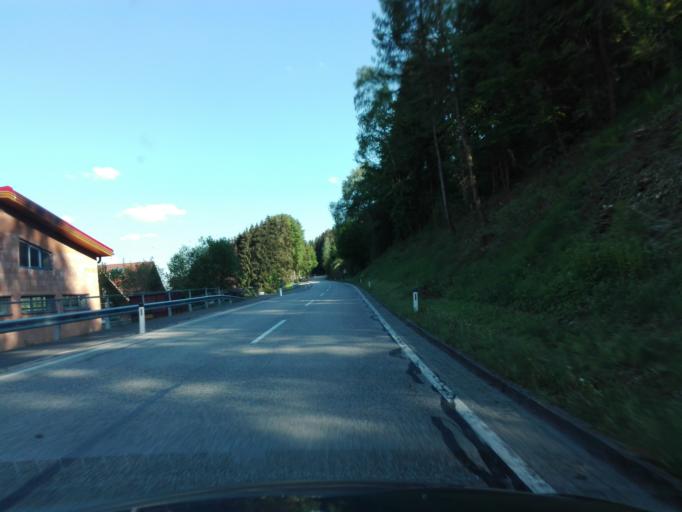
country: AT
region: Upper Austria
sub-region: Politischer Bezirk Rohrbach
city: Pfarrkirchen im Muehlkreis
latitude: 48.4899
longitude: 13.7440
